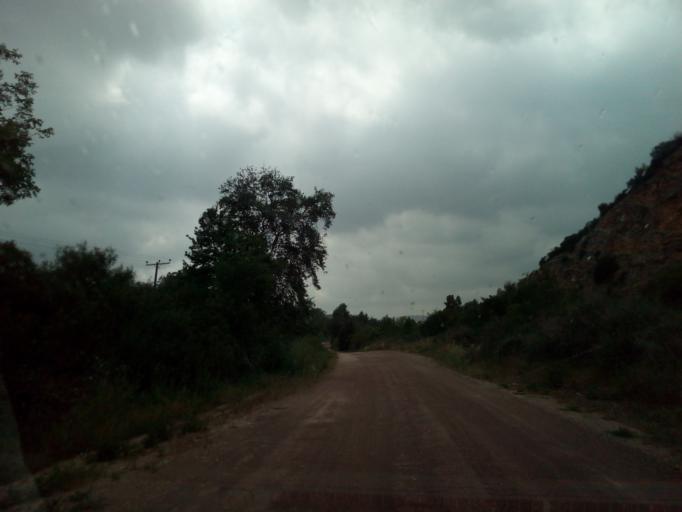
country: CY
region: Pafos
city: Mesogi
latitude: 34.8051
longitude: 32.6109
